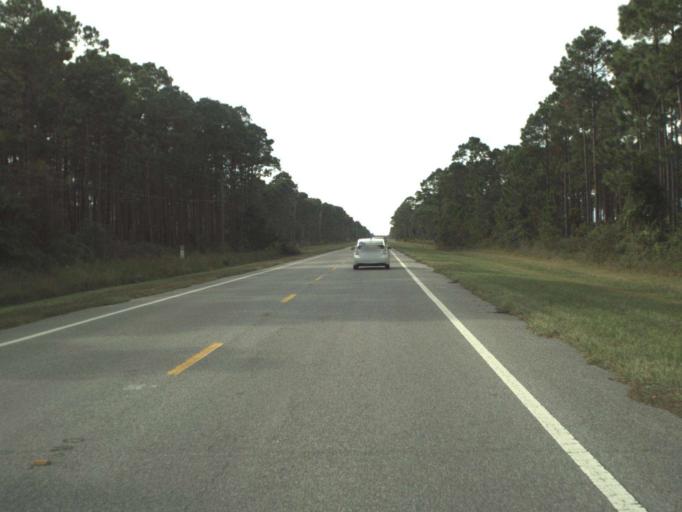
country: US
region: Florida
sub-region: Bay County
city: Tyndall Air Force Base
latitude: 30.0465
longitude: -85.5597
